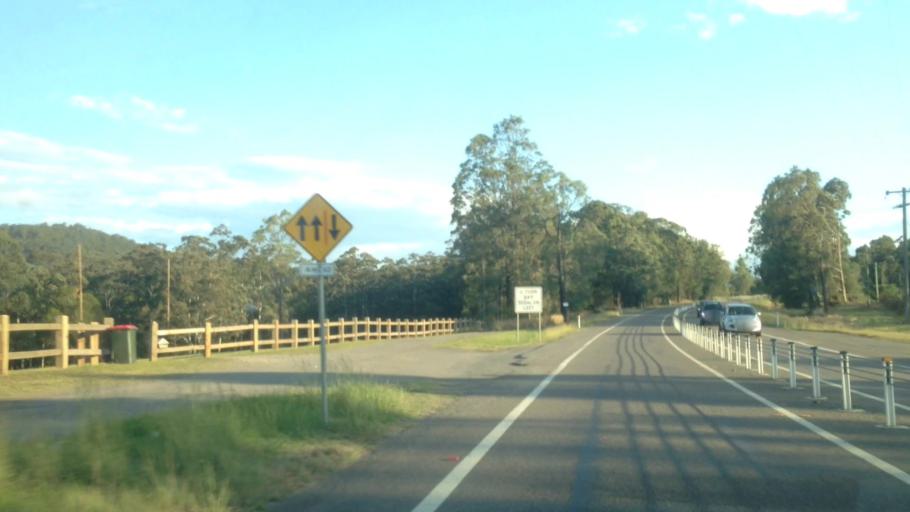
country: AU
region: New South Wales
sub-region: Lake Macquarie Shire
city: Holmesville
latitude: -32.9549
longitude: 151.4809
